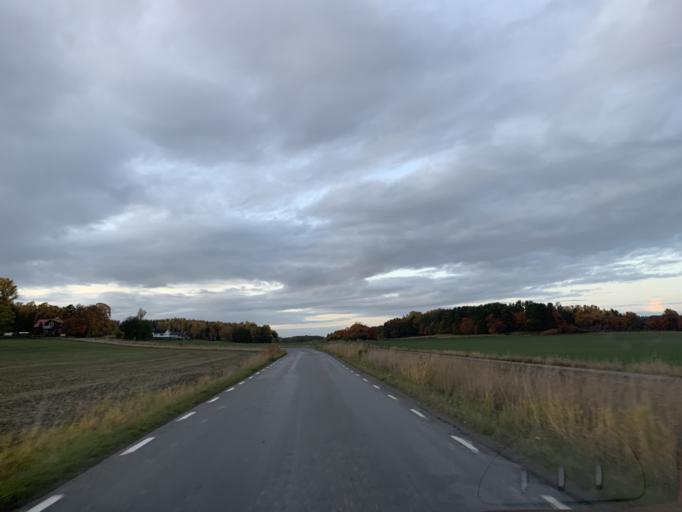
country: SE
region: Stockholm
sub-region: Nynashamns Kommun
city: Osmo
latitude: 58.9118
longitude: 17.7855
